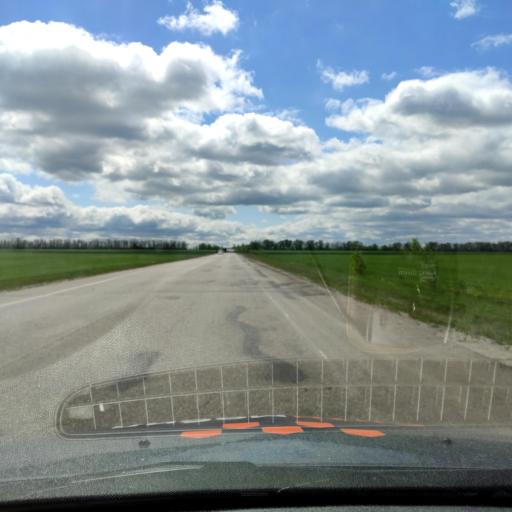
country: RU
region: Voronezj
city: Novaya Usman'
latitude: 51.5968
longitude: 39.3385
